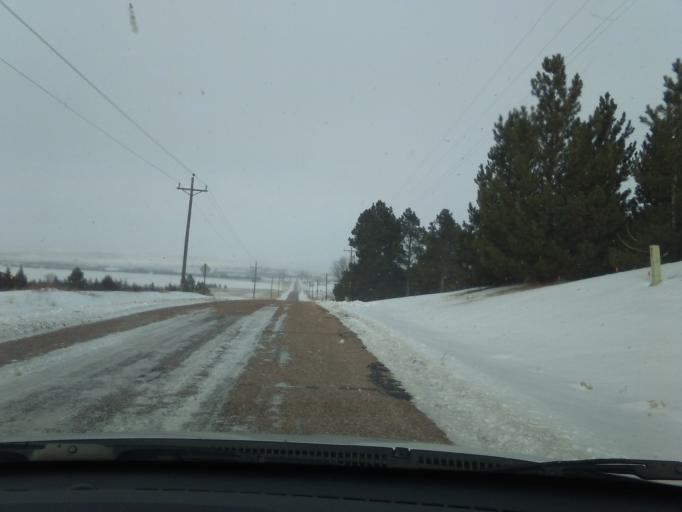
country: US
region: Nebraska
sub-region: Kimball County
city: Kimball
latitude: 41.2245
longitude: -103.6245
